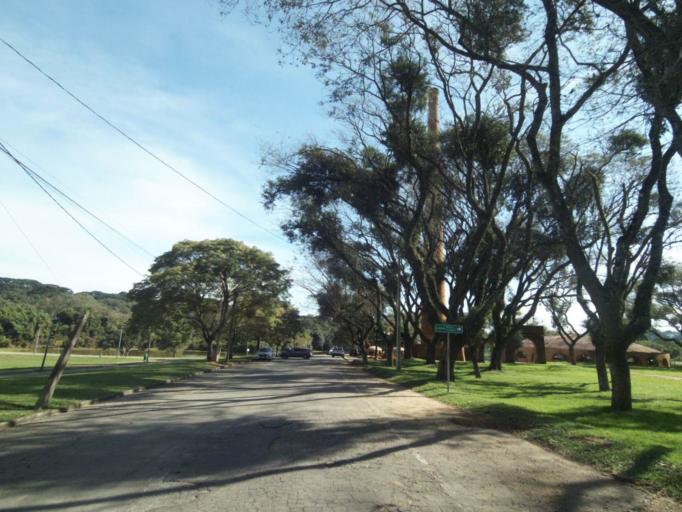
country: BR
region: Parana
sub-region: Curitiba
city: Curitiba
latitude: -25.4211
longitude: -49.3058
